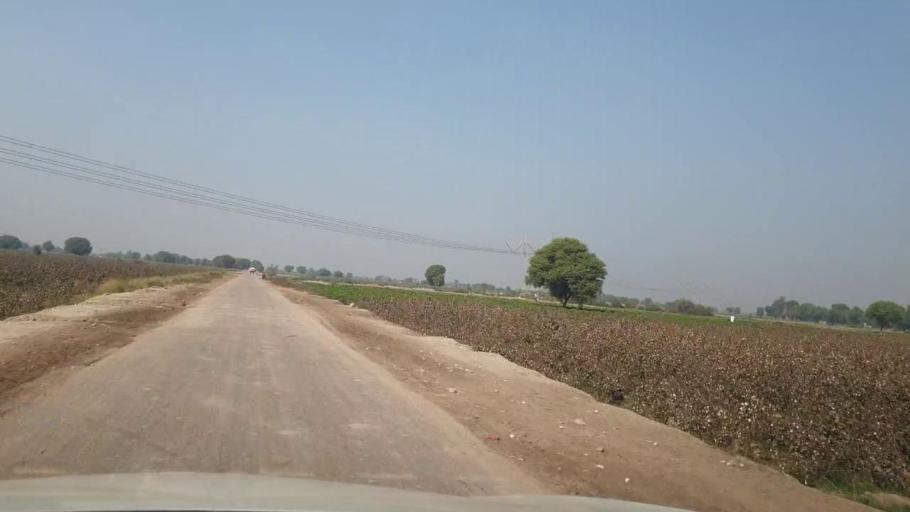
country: PK
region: Sindh
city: Bhan
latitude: 26.5337
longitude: 67.7501
